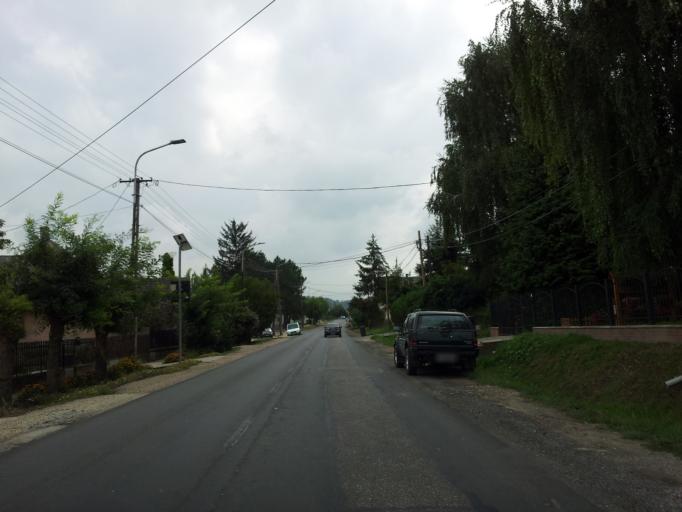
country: HU
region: Tolna
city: Tamasi
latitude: 46.6254
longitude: 18.2899
